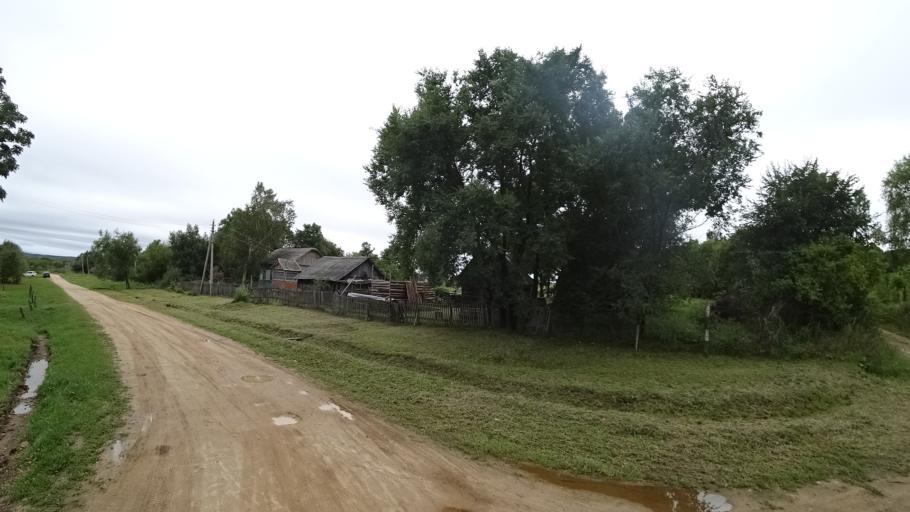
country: RU
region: Primorskiy
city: Rettikhovka
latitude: 44.1407
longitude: 132.6368
